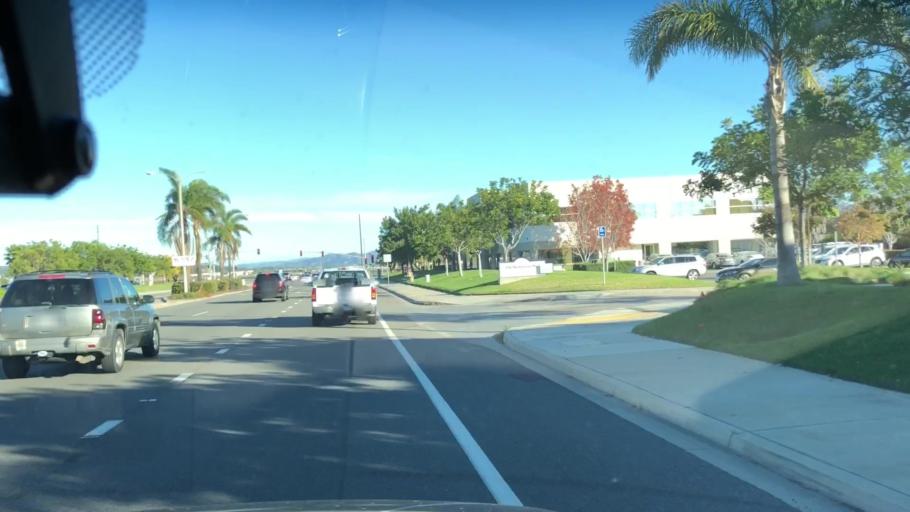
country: US
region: California
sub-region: Ventura County
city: El Rio
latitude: 34.2187
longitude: -119.1444
